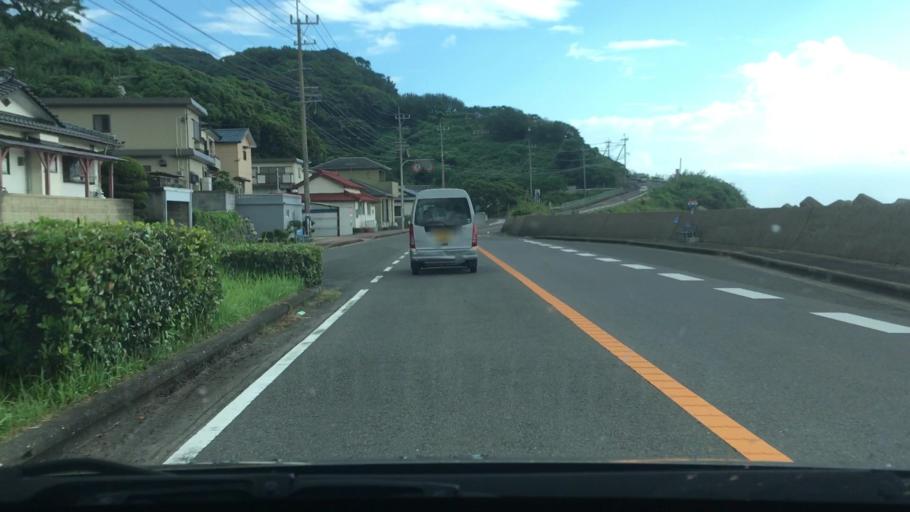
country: JP
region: Nagasaki
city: Togitsu
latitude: 32.8756
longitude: 129.6795
